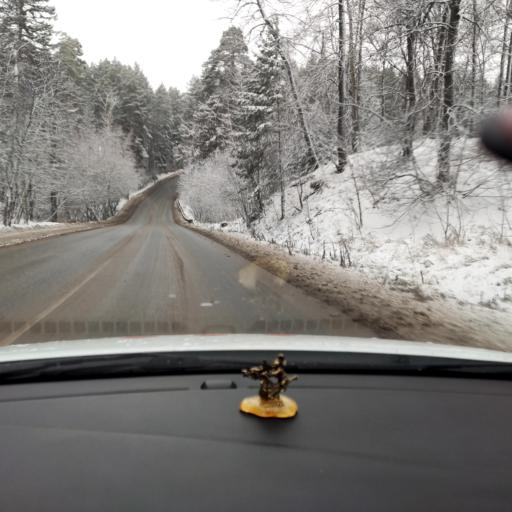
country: RU
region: Tatarstan
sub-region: Zelenodol'skiy Rayon
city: Zelenodolsk
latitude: 55.8601
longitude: 48.5343
